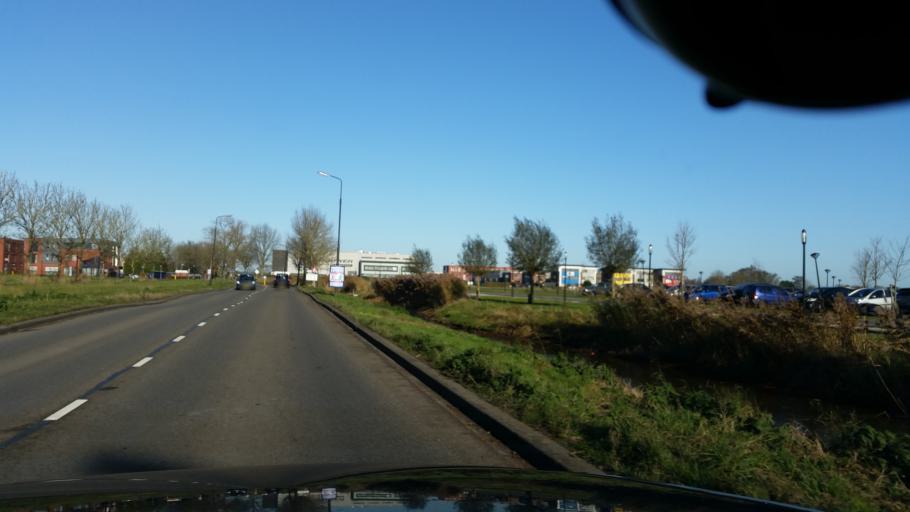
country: NL
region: Utrecht
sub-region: Gemeente De Ronde Venen
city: Mijdrecht
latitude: 52.2087
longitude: 4.8868
